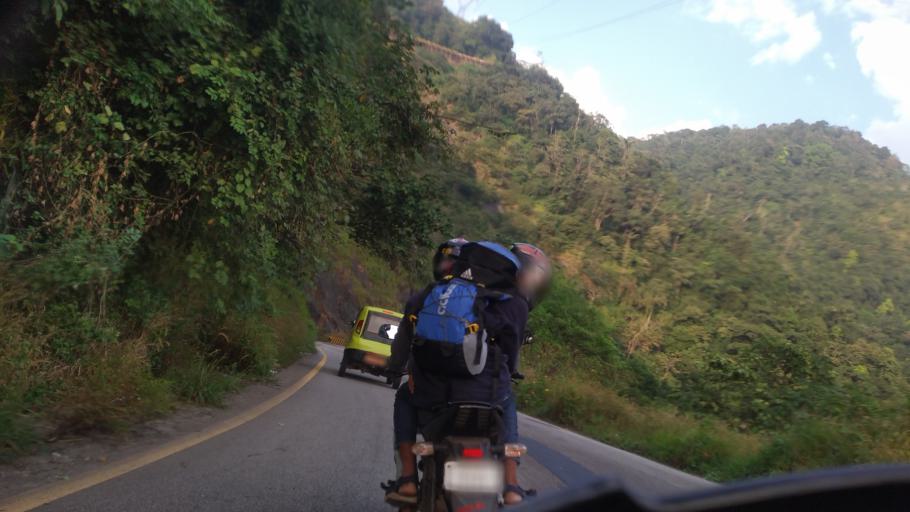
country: IN
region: Kerala
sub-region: Wayanad
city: Kalpetta
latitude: 11.5100
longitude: 76.0191
